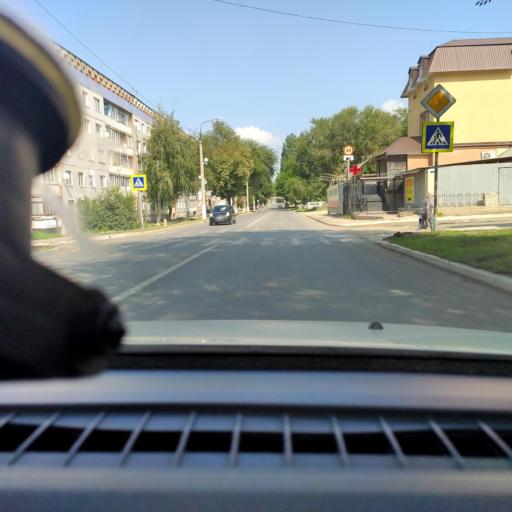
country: RU
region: Samara
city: Chapayevsk
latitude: 52.9591
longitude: 49.6831
